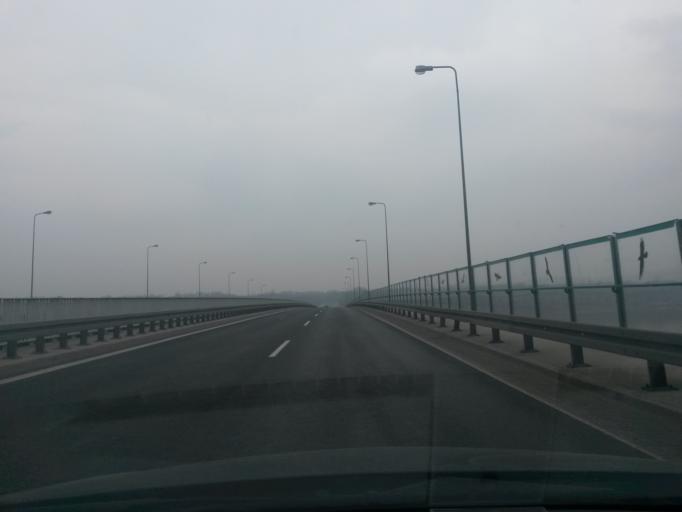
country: PL
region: Masovian Voivodeship
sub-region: Powiat legionowski
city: Nieporet
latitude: 52.4564
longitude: 21.0166
